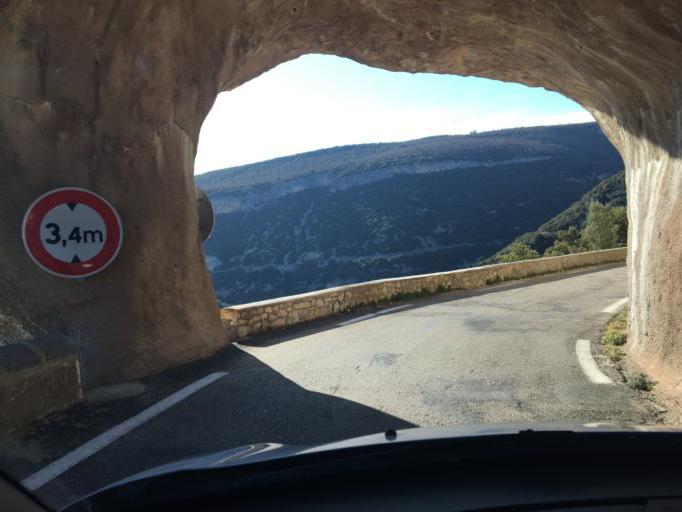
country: FR
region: Provence-Alpes-Cote d'Azur
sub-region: Departement du Vaucluse
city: Villes-sur-Auzon
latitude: 44.0636
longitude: 5.3144
